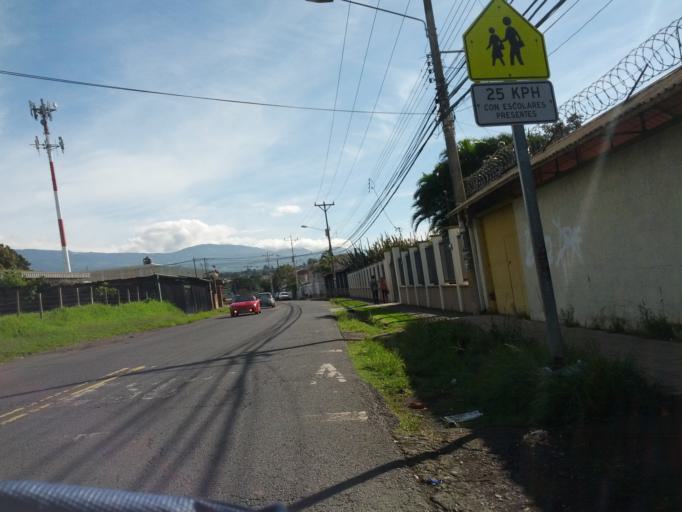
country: CR
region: Alajuela
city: Alajuela
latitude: 10.0181
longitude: -84.2024
